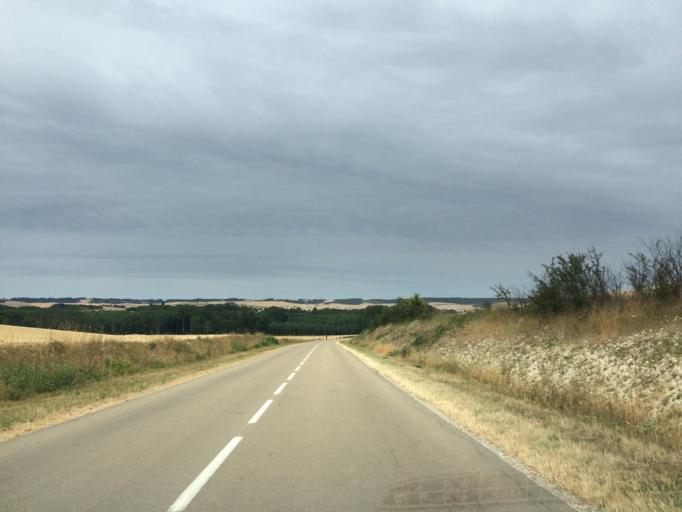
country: FR
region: Bourgogne
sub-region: Departement de l'Yonne
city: Aillant-sur-Tholon
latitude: 47.8536
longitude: 3.3661
